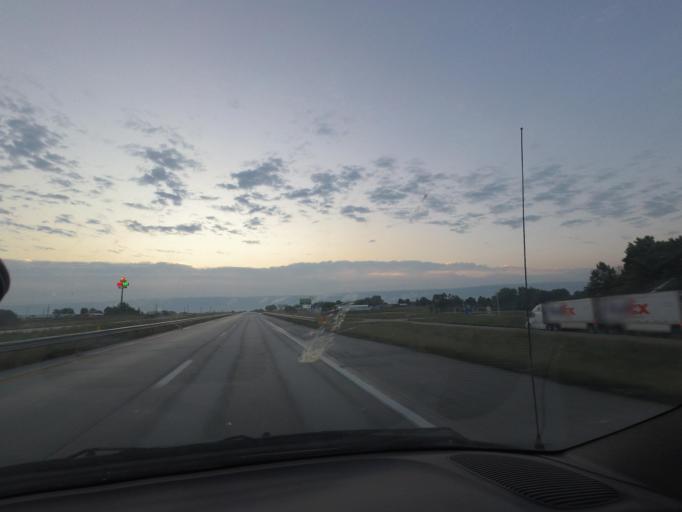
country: US
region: Missouri
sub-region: Macon County
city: Macon
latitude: 39.7603
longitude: -92.5664
